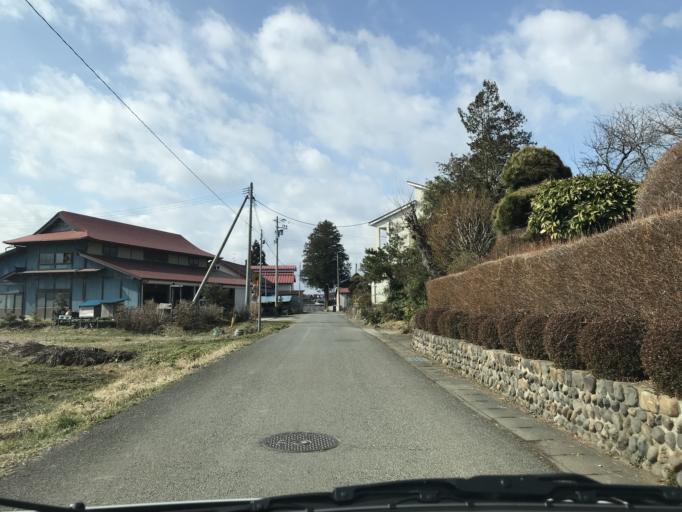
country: JP
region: Iwate
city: Mizusawa
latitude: 39.0457
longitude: 141.1438
